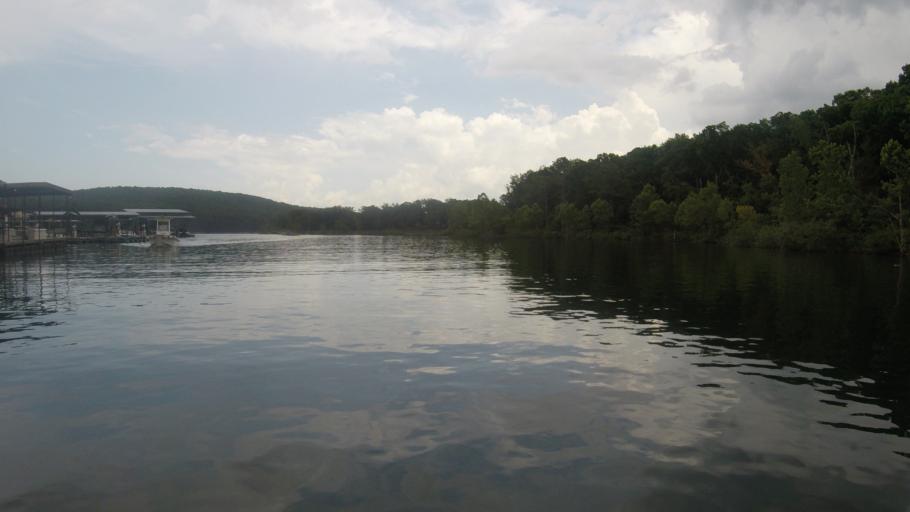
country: US
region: Missouri
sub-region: Barry County
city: Shell Knob
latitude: 36.5942
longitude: -93.5489
